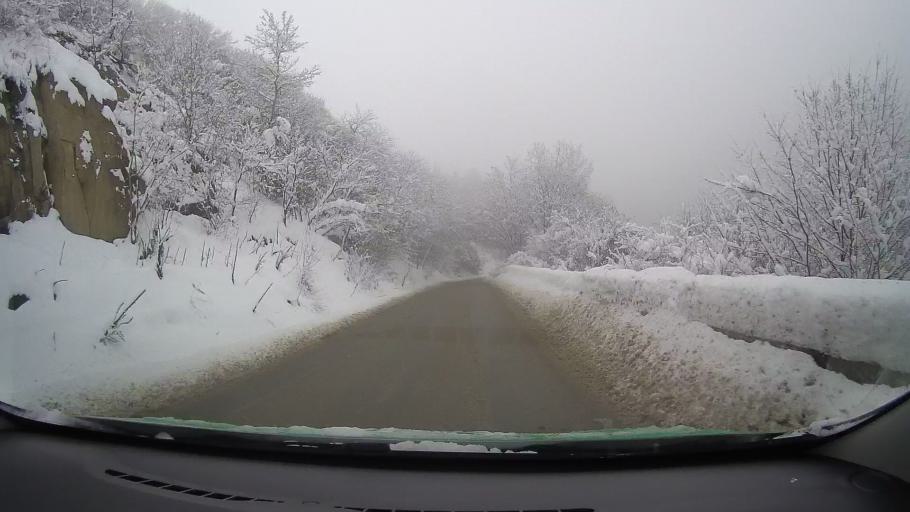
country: RO
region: Sibiu
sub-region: Comuna Tilisca
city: Tilisca
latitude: 45.7983
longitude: 23.7936
